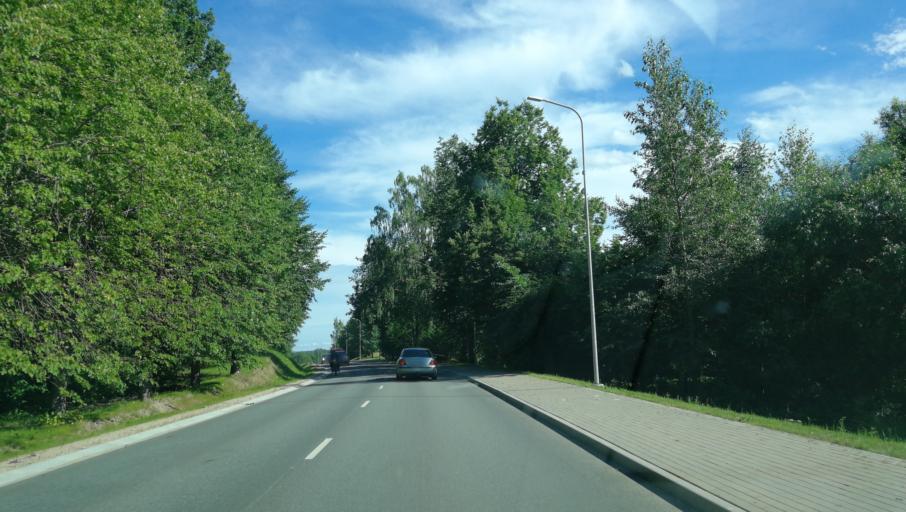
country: LV
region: Cesvaine
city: Cesvaine
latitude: 56.9664
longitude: 26.3185
